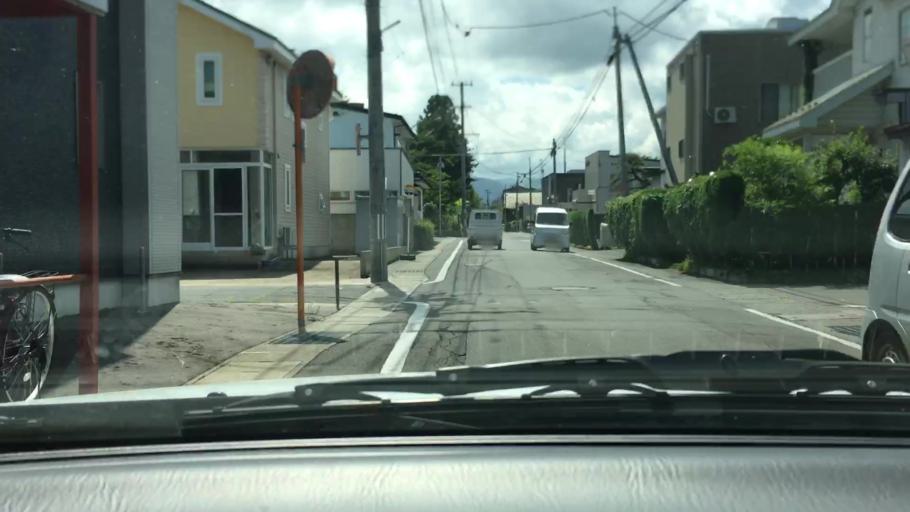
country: JP
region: Aomori
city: Hirosaki
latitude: 40.5910
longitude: 140.4710
